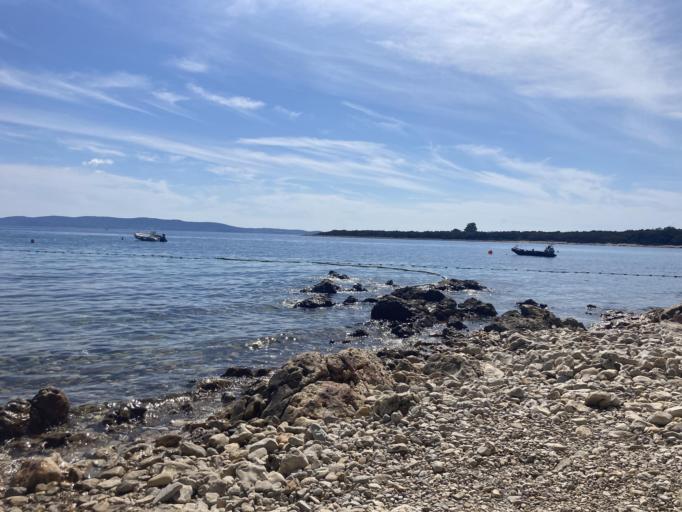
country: HR
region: Primorsko-Goranska
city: Mali Losinj
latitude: 44.6126
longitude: 14.5106
